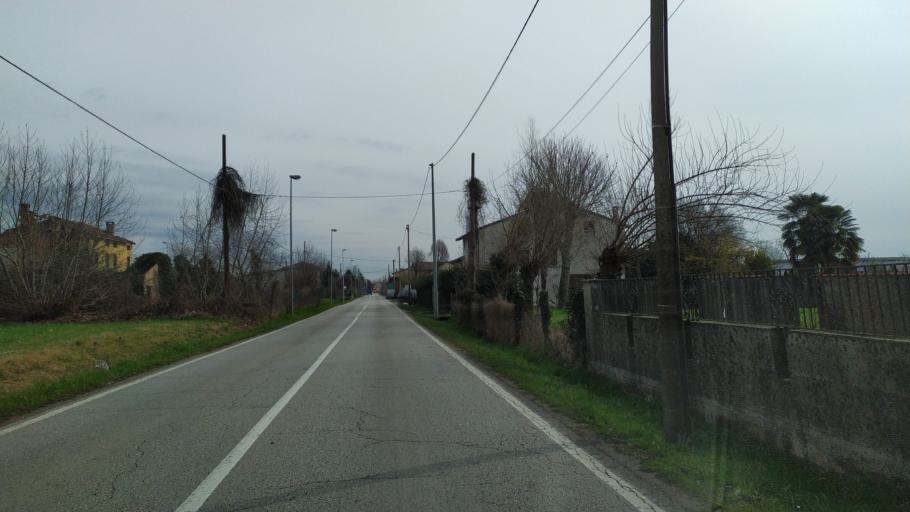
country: IT
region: Veneto
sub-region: Provincia di Vicenza
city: Dueville
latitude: 45.6409
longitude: 11.5344
